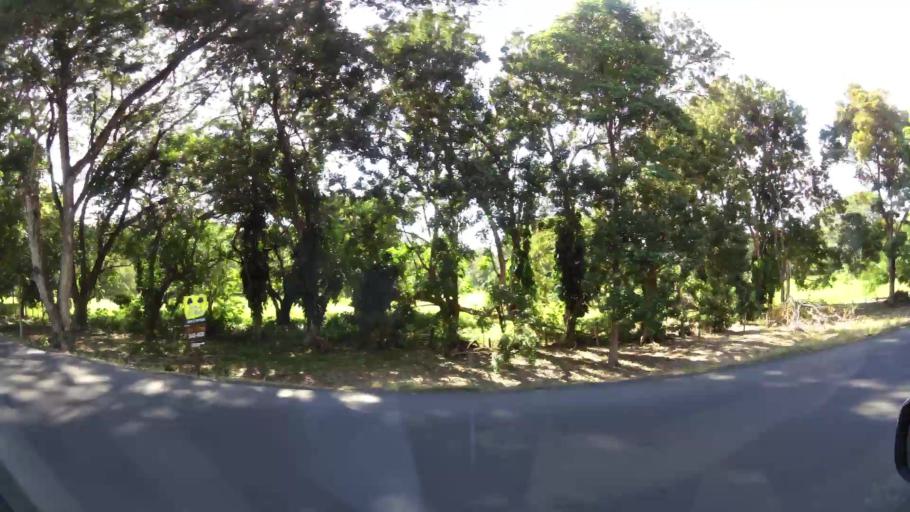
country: CR
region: Puntarenas
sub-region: Canton de Garabito
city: Jaco
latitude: 9.6076
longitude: -84.6157
